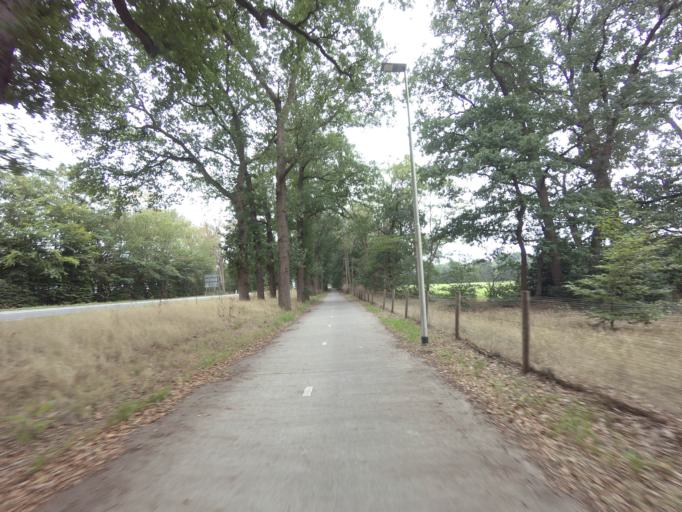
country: NL
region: North Holland
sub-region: Gemeente Wijdemeren
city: Nieuw-Loosdrecht
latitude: 52.1810
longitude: 5.1769
